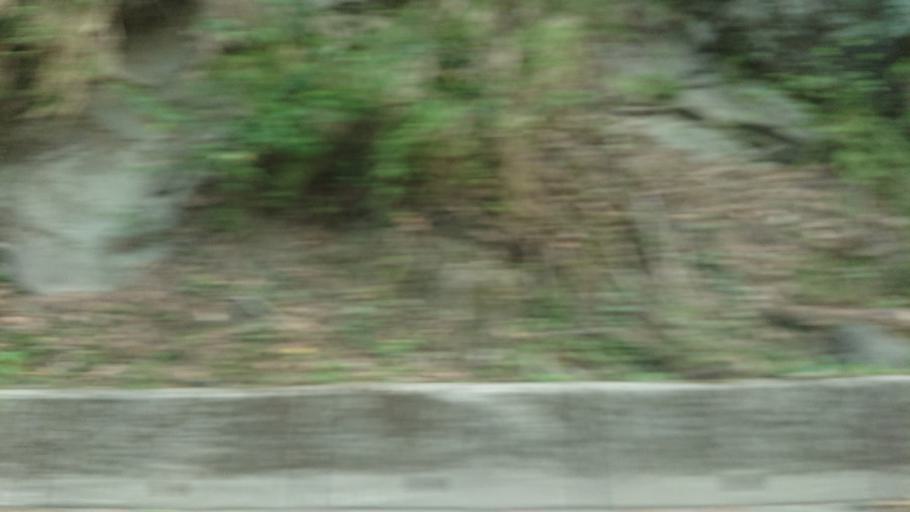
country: TW
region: Taiwan
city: Daxi
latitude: 24.8750
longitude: 121.3840
